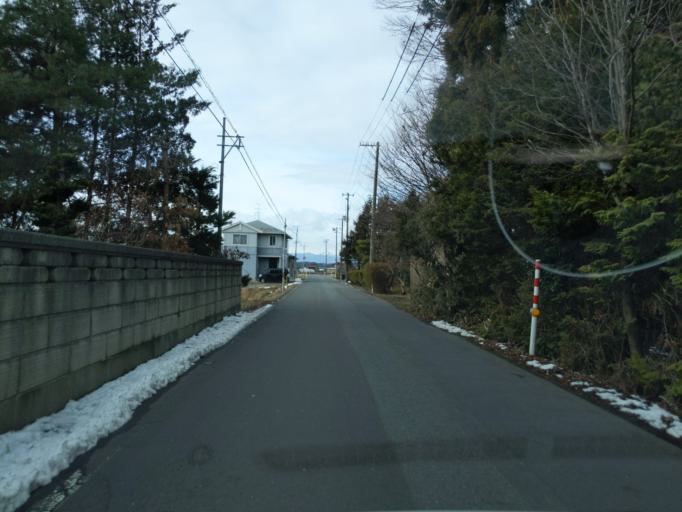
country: JP
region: Iwate
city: Mizusawa
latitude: 39.0920
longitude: 141.1726
